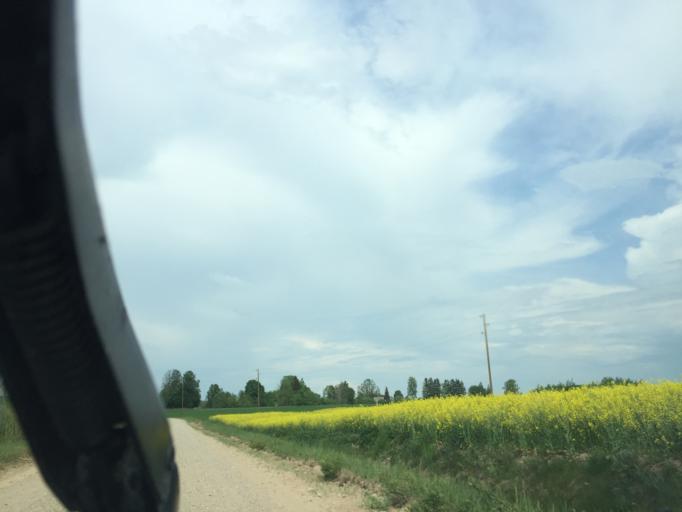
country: LV
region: Livani
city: Livani
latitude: 56.5789
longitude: 26.1793
